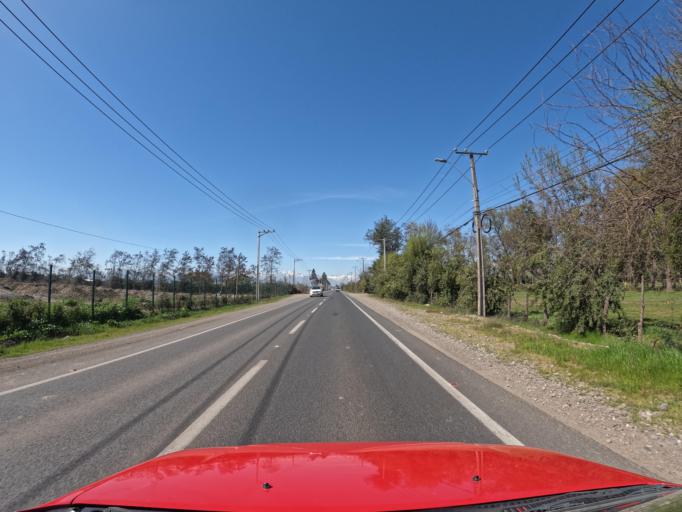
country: CL
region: Maule
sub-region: Provincia de Curico
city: Teno
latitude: -34.9608
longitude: -71.1022
